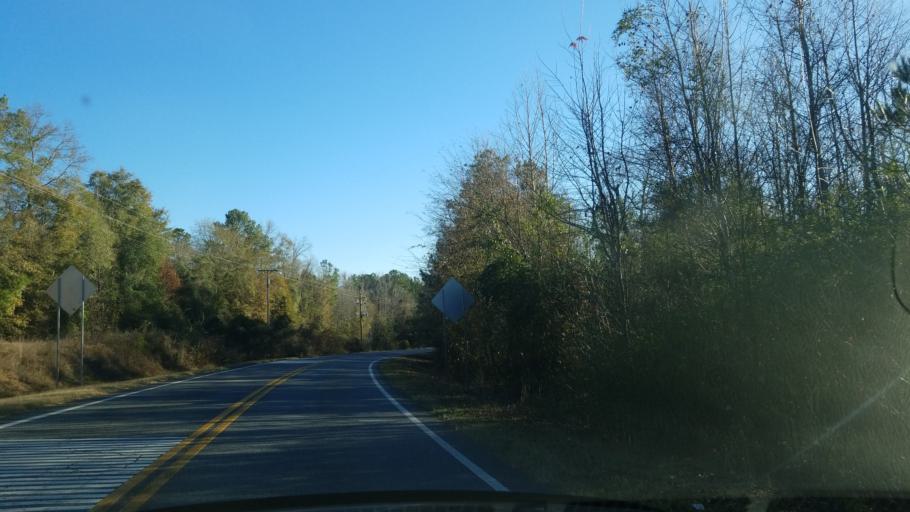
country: US
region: Georgia
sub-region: Talbot County
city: Talbotton
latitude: 32.5625
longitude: -84.6050
